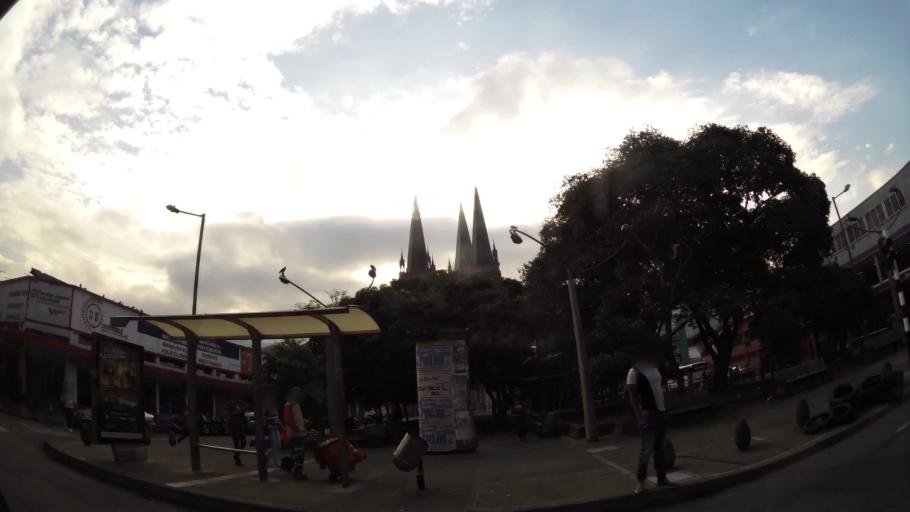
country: CO
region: Antioquia
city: Medellin
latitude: 6.2367
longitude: -75.5738
